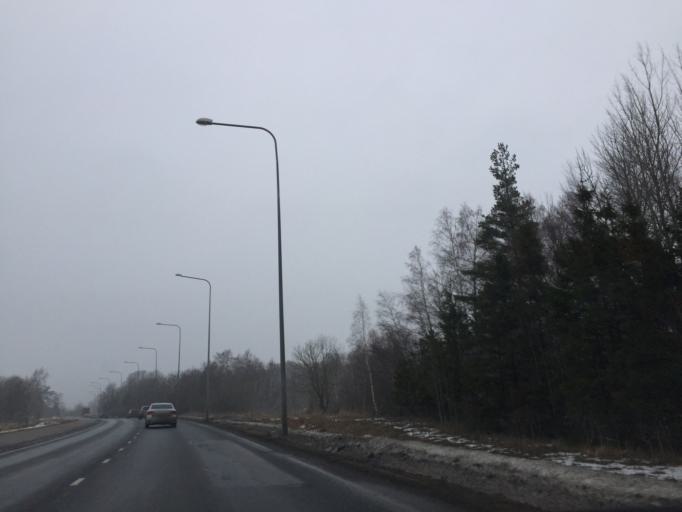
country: EE
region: Laeaene
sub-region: Lihula vald
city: Lihula
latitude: 58.5756
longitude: 23.5239
